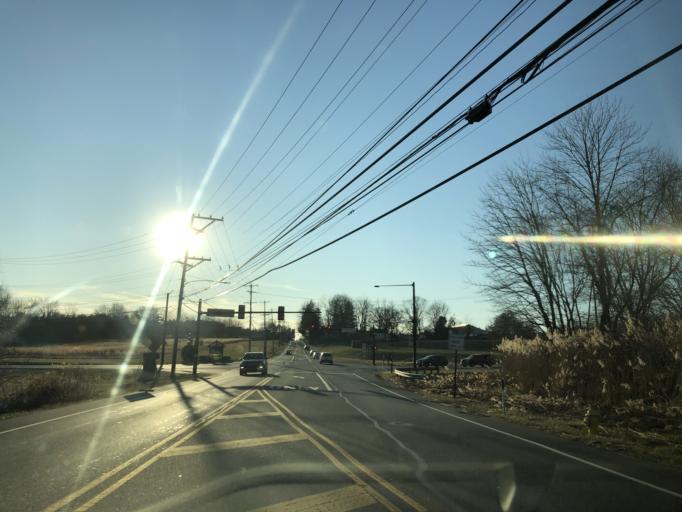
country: US
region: Pennsylvania
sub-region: Delaware County
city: Chester Heights
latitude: 39.8692
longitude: -75.5077
